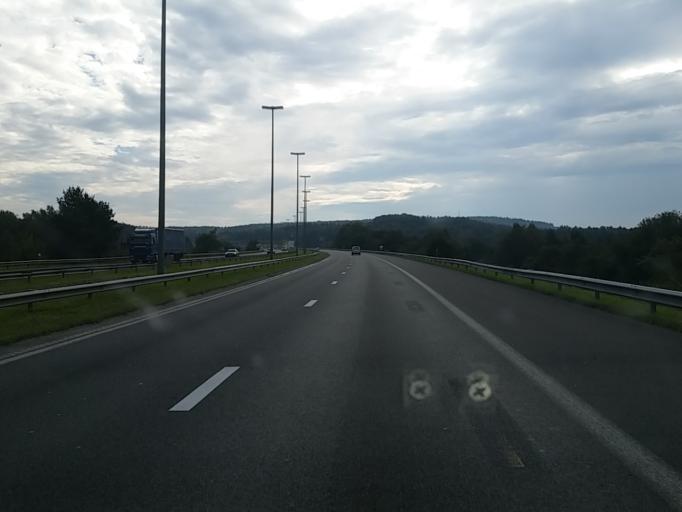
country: BE
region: Wallonia
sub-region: Province du Luxembourg
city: Arlon
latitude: 49.6763
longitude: 5.7645
